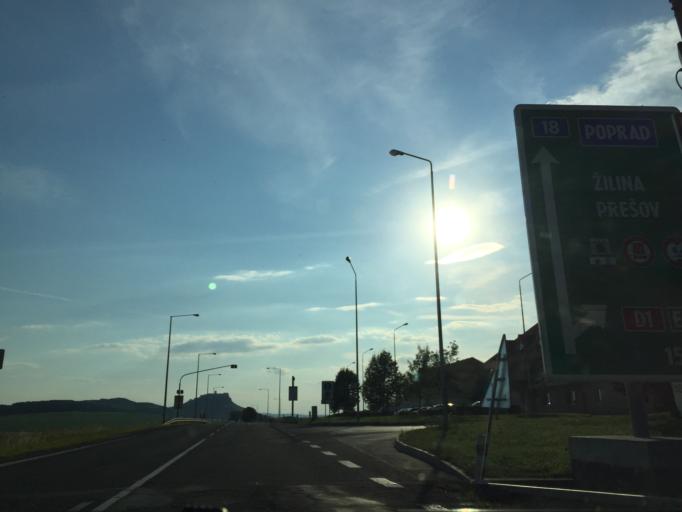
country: SK
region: Presovsky
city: Spisske Podhradie
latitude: 49.0067
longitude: 20.8134
